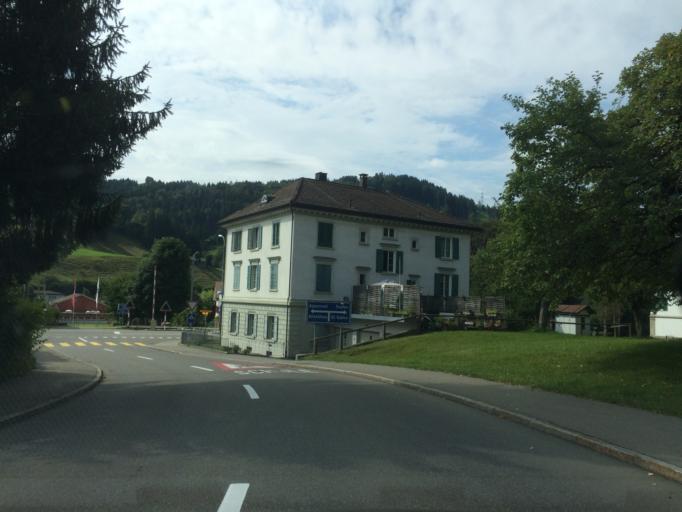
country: CH
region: Appenzell Ausserrhoden
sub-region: Bezirk Mittelland
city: Buhler
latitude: 47.3736
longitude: 9.4245
